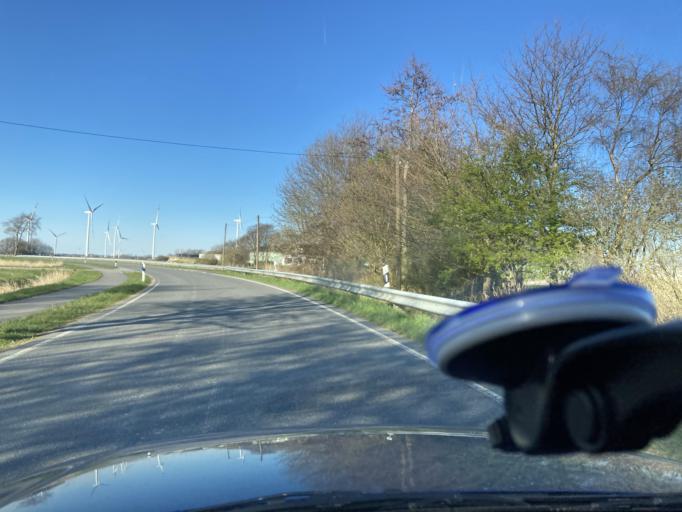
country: DE
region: Schleswig-Holstein
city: Wesselburen
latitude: 54.2244
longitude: 8.9493
